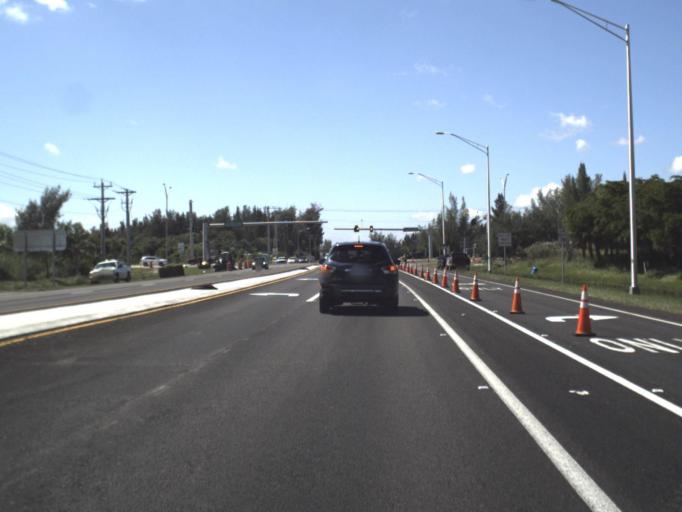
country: US
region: Florida
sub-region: Lee County
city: Pine Island Center
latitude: 26.6376
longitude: -82.0382
